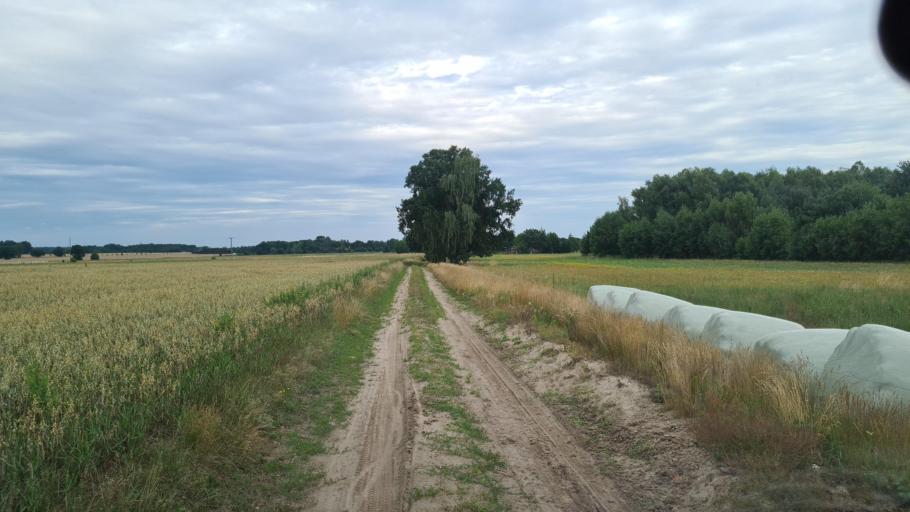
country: DE
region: Brandenburg
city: Crinitz
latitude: 51.7172
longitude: 13.8333
